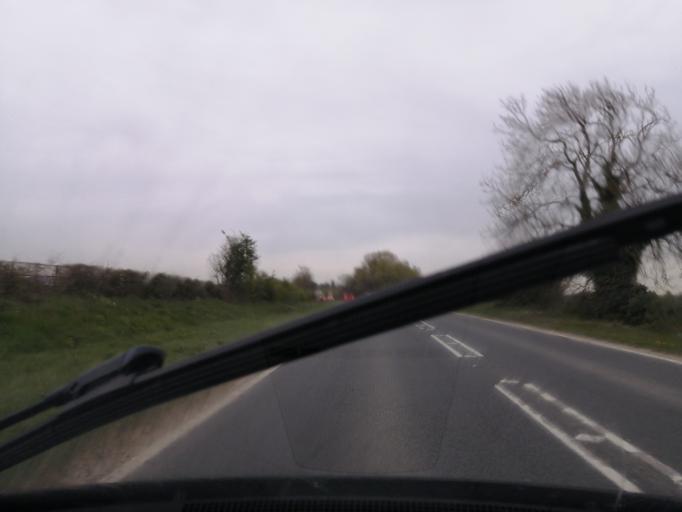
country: GB
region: England
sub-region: Peterborough
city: Thornhaugh
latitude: 52.5846
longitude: -0.4314
